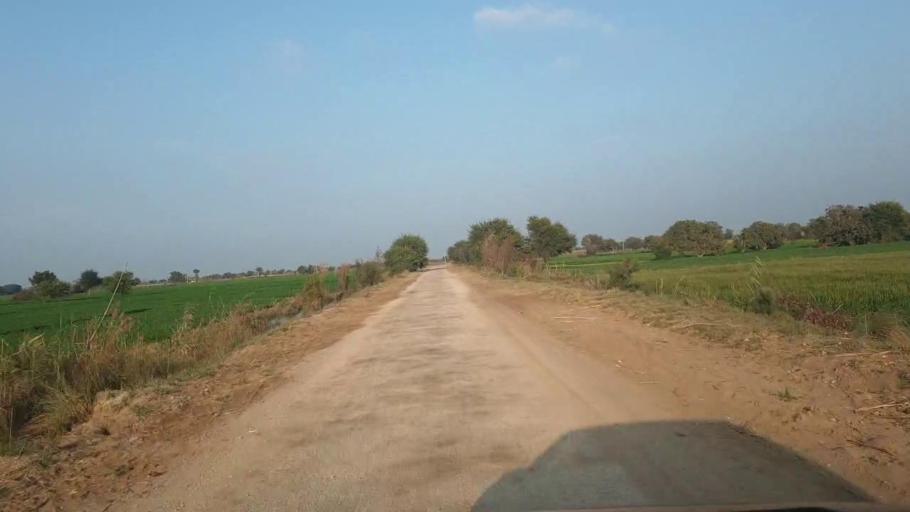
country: PK
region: Sindh
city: Berani
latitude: 25.8550
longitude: 68.7341
